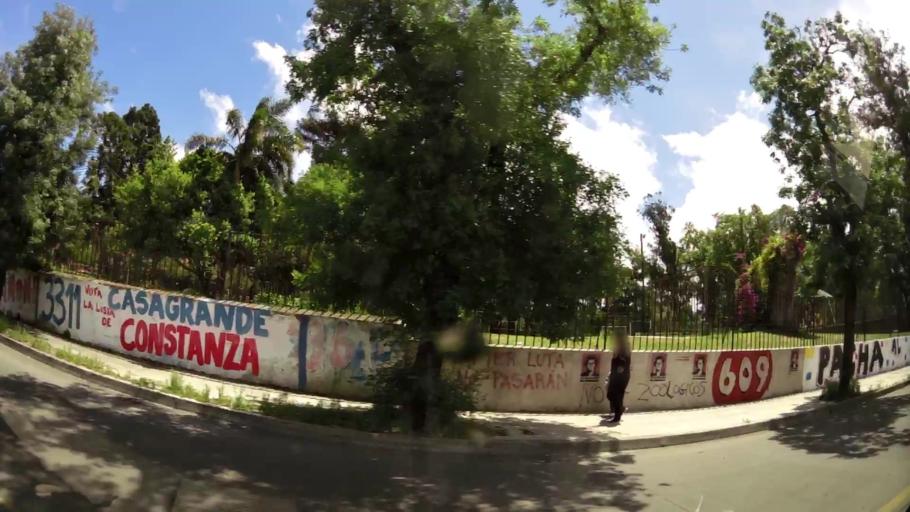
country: UY
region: Montevideo
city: Montevideo
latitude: -34.8599
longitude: -56.1856
